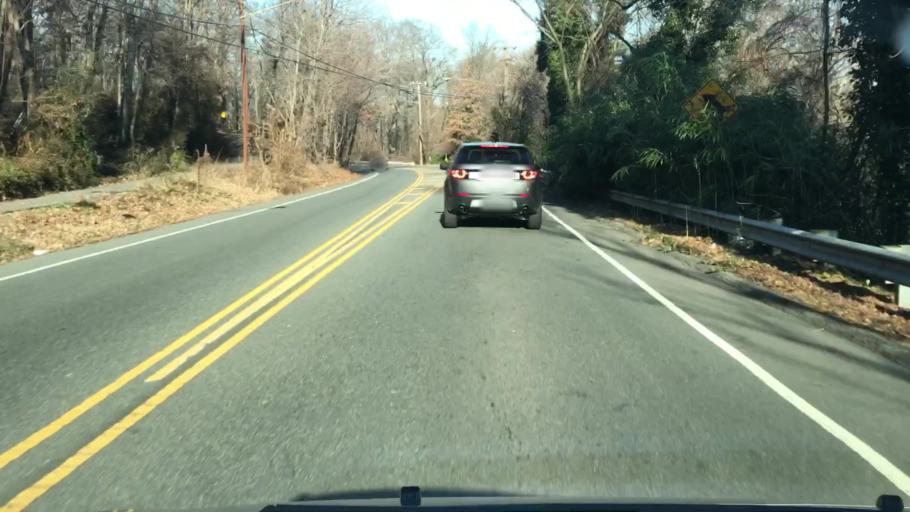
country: US
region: Virginia
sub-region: Fairfax County
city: Belle Haven
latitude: 38.7669
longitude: -77.0603
